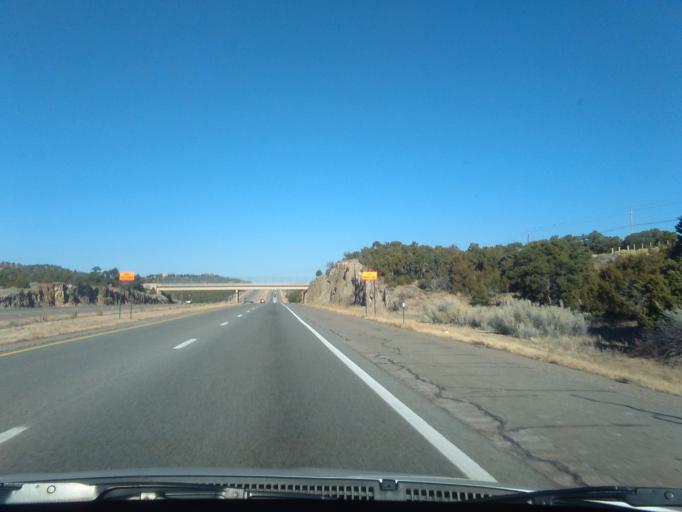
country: US
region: New Mexico
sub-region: Santa Fe County
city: Eldorado at Santa Fe
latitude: 35.6036
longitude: -105.9107
